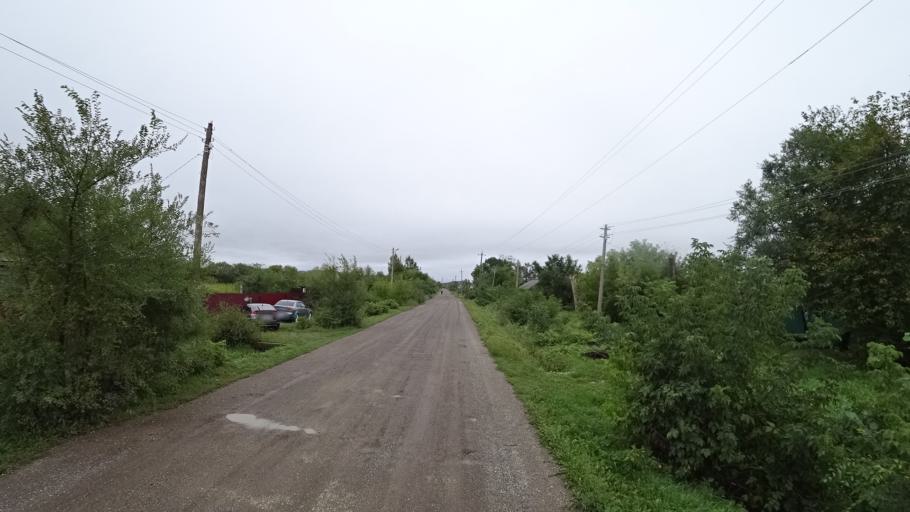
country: RU
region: Primorskiy
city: Monastyrishche
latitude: 44.1992
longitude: 132.4538
